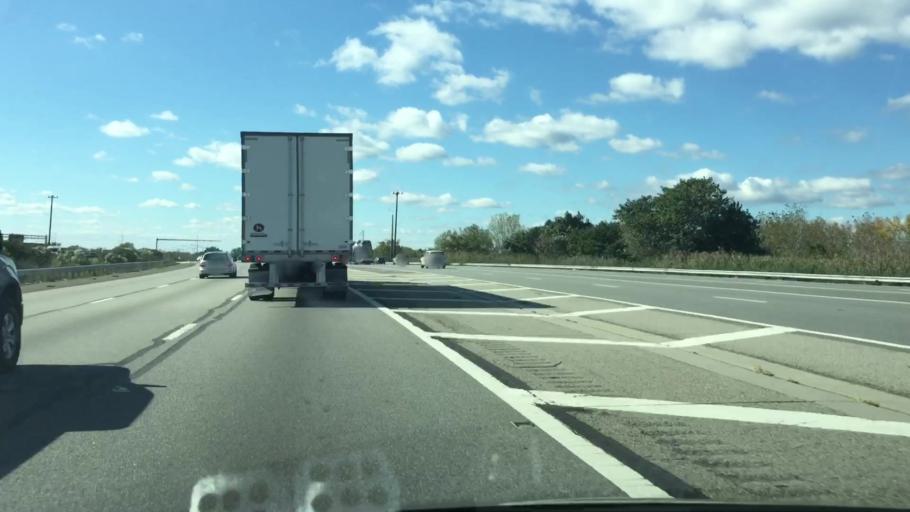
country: US
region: Pennsylvania
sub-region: Delaware County
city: Colwyn
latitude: 39.8936
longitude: -75.2324
